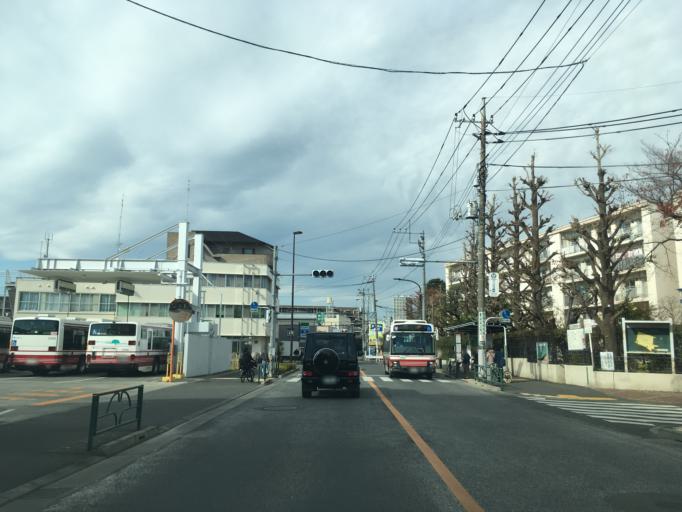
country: JP
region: Tokyo
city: Chofugaoka
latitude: 35.6428
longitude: 139.5677
